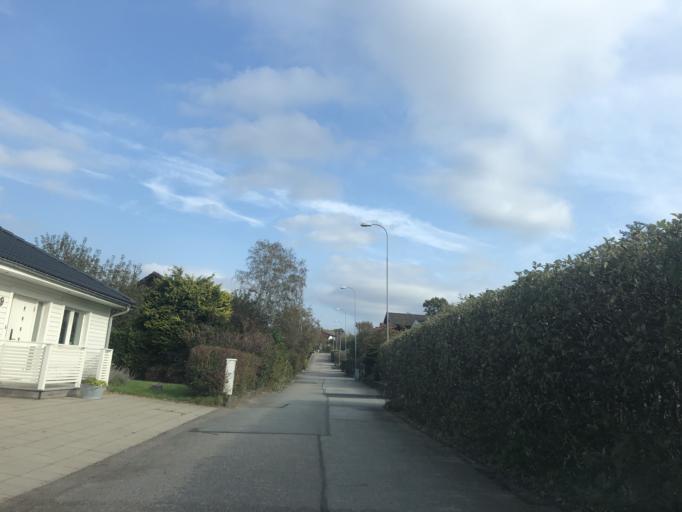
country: SE
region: Vaestra Goetaland
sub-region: Goteborg
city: Majorna
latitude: 57.6535
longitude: 11.8835
